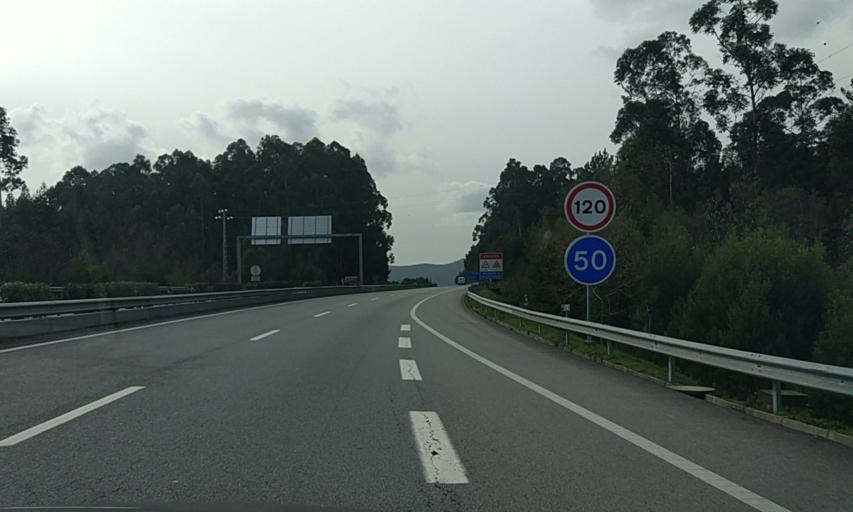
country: PT
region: Porto
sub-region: Paredes
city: Baltar
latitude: 41.1681
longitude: -8.3901
